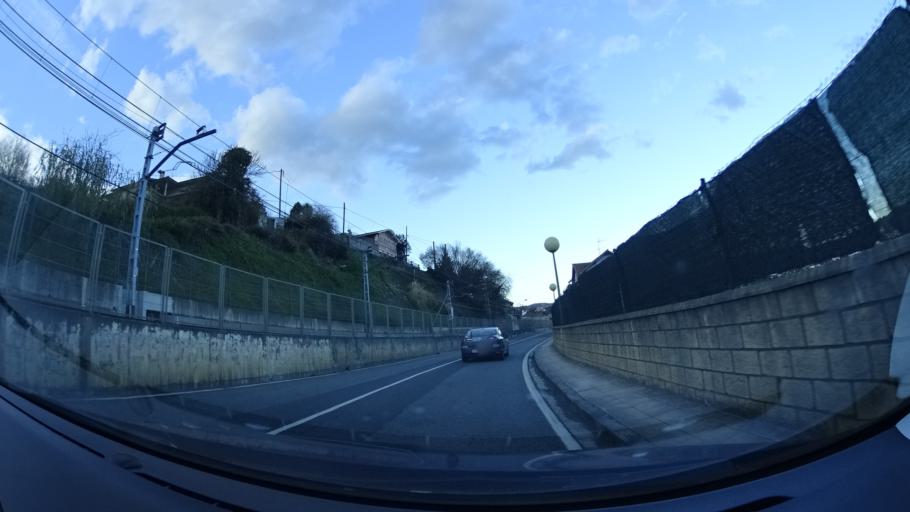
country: ES
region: Basque Country
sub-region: Bizkaia
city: Plentzia
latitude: 43.3986
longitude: -2.9467
